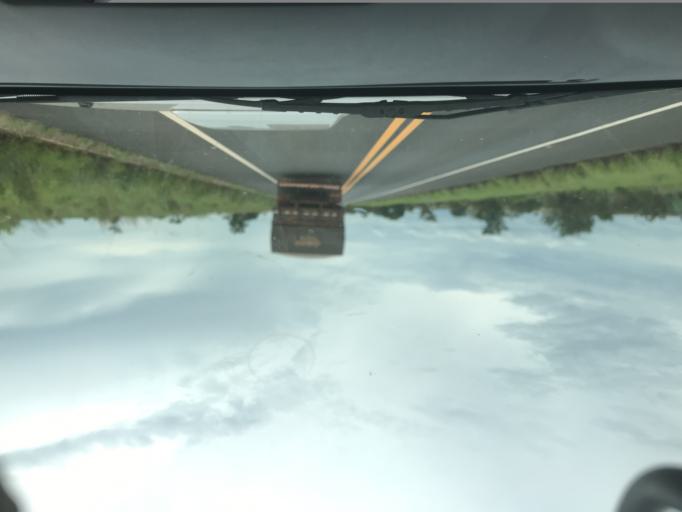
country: BR
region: Minas Gerais
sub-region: Araxa
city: Araxa
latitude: -19.3684
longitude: -46.8551
